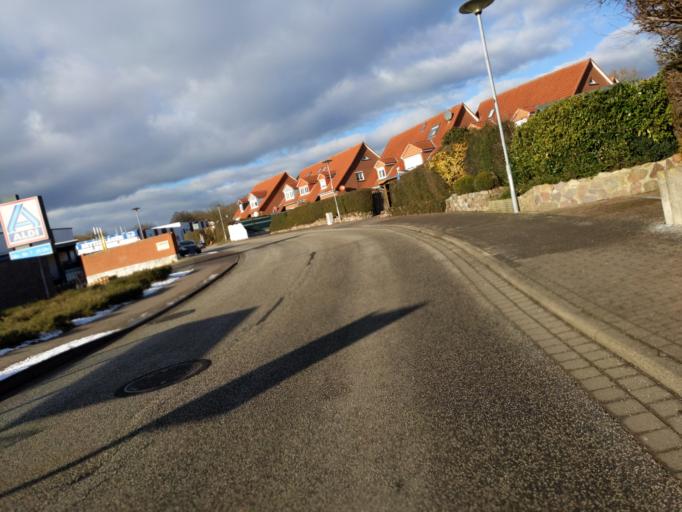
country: DE
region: Schleswig-Holstein
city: Travemuende
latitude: 53.9634
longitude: 10.8613
